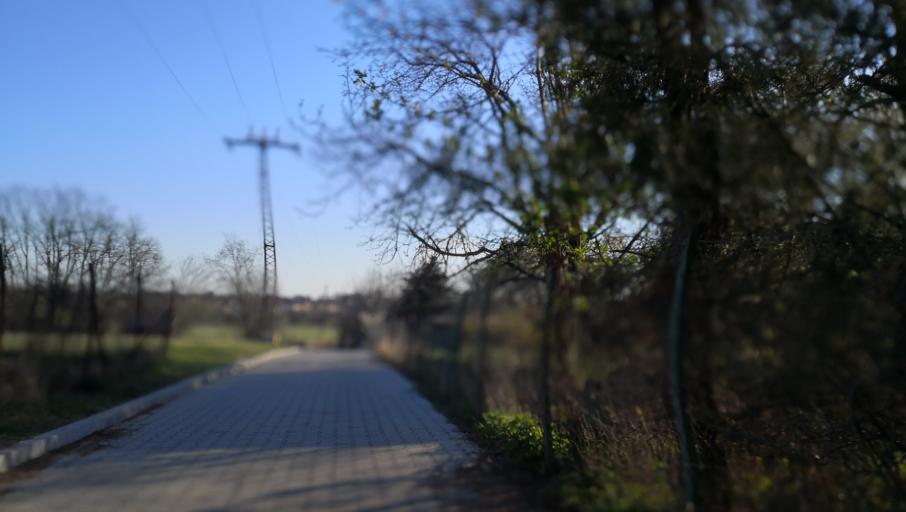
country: HU
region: Pest
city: Csomor
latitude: 47.5164
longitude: 19.2310
